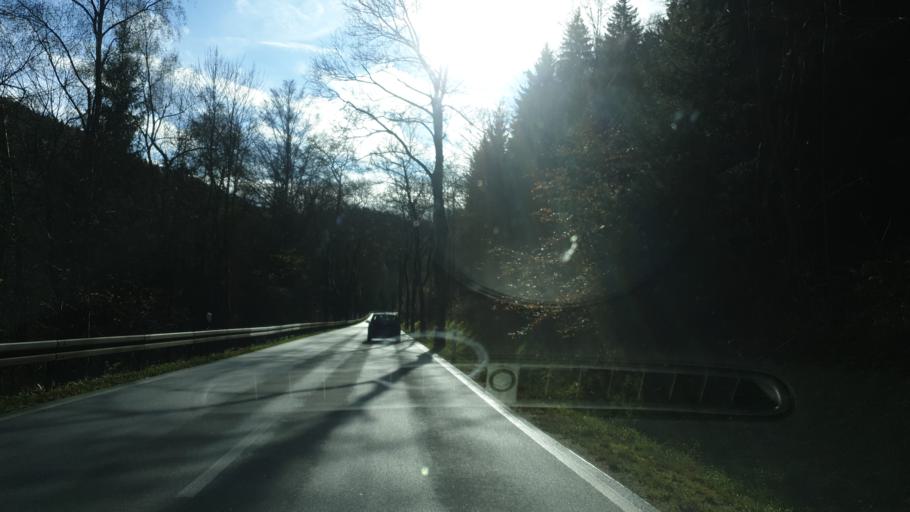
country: DE
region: Saxony
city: Sosa
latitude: 50.5326
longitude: 12.6502
